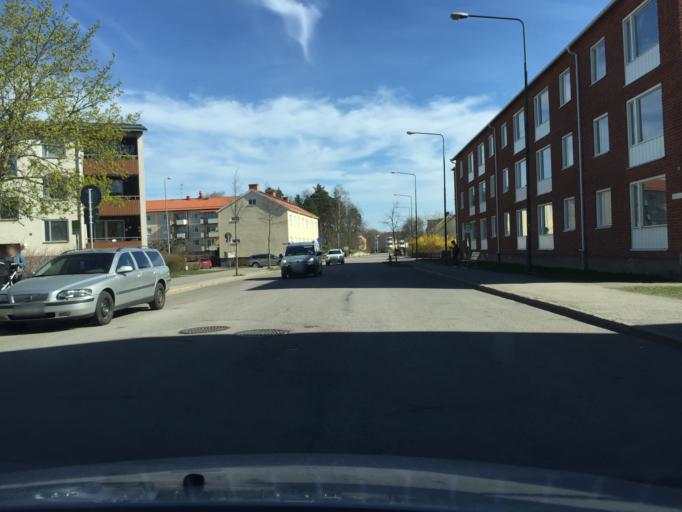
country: SE
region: Soedermanland
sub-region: Katrineholms Kommun
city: Katrineholm
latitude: 58.9945
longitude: 16.2181
